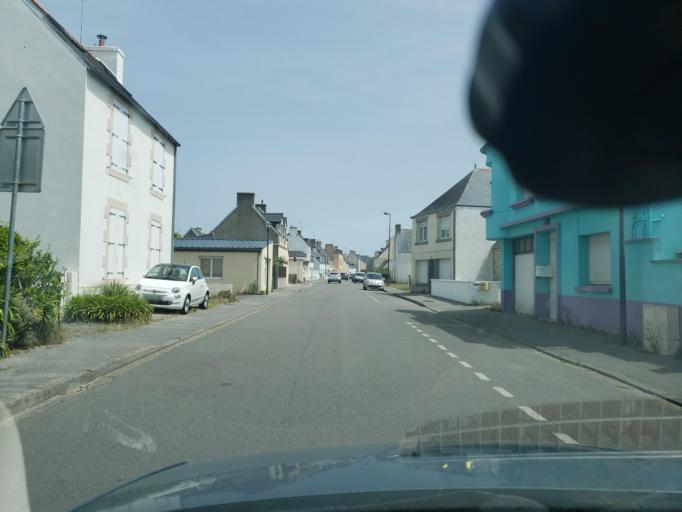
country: FR
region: Brittany
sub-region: Departement du Finistere
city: Guilvinec
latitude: 47.7993
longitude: -4.2900
